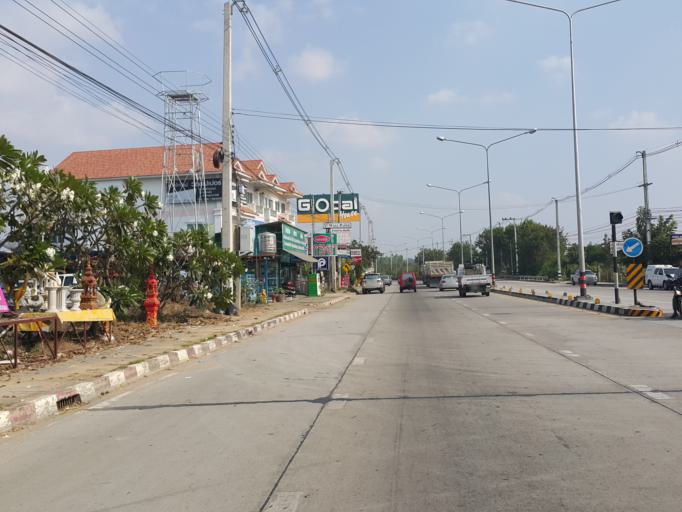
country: TH
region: Chiang Mai
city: Saraphi
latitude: 18.7430
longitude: 98.9987
